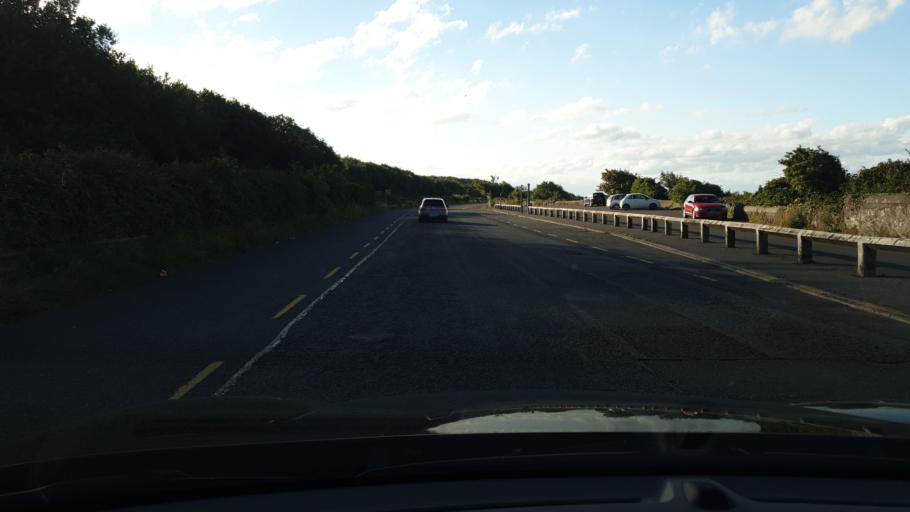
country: IE
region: Leinster
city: Balrothery
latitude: 53.5864
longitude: -6.1504
